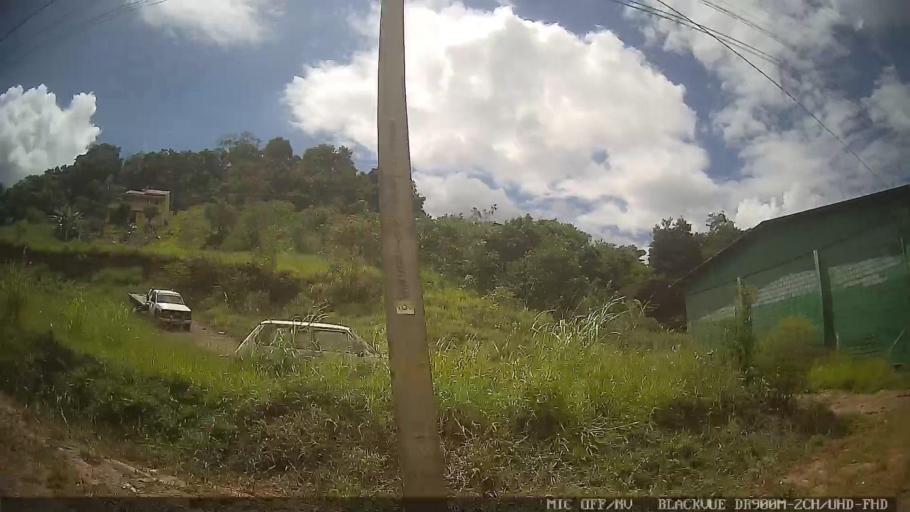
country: BR
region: Minas Gerais
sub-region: Extrema
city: Extrema
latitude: -22.7888
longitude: -46.4438
